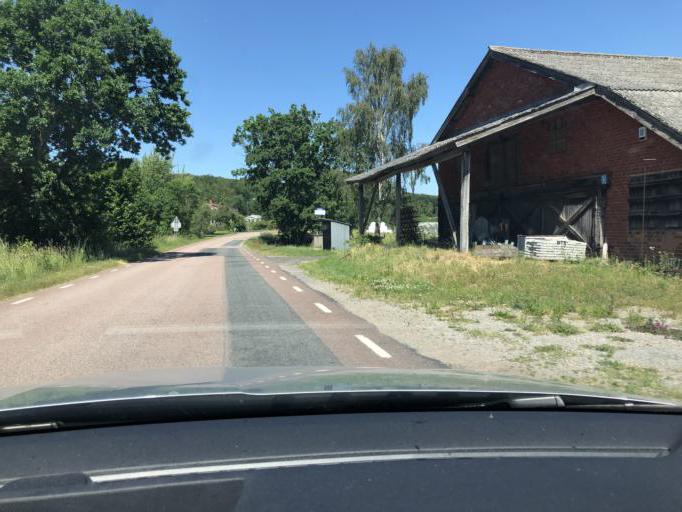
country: SE
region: Blekinge
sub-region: Olofstroms Kommun
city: Jamshog
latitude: 56.1612
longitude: 14.5992
